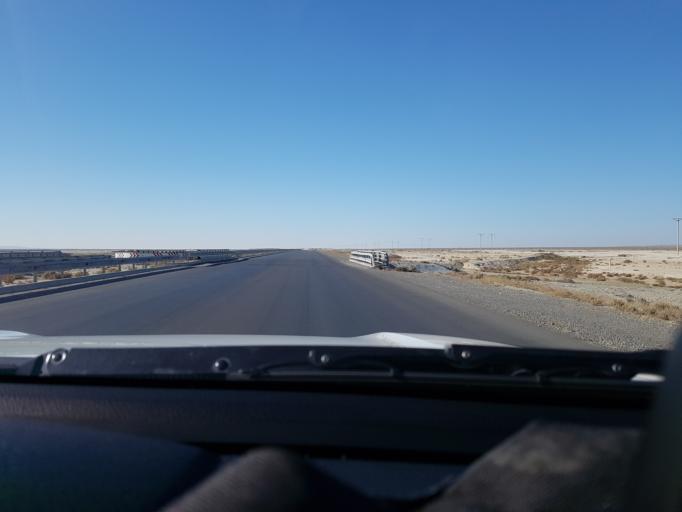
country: TM
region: Balkan
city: Gazanjyk
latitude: 39.2604
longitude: 55.1130
